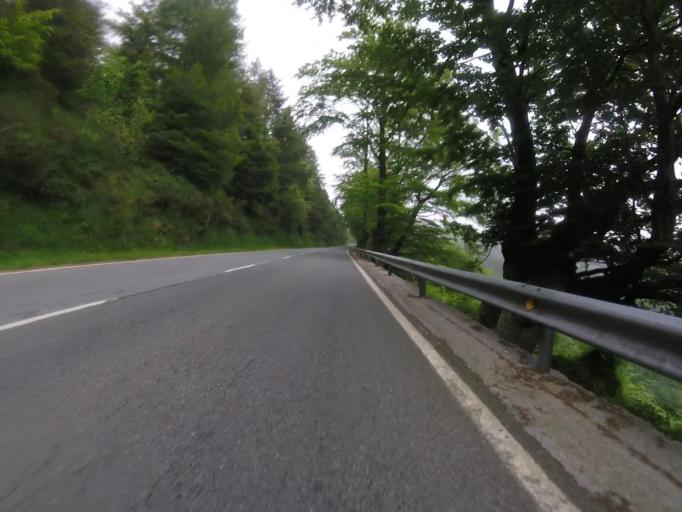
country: ES
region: Navarre
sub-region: Provincia de Navarra
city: Zugarramurdi
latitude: 43.2476
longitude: -1.4830
